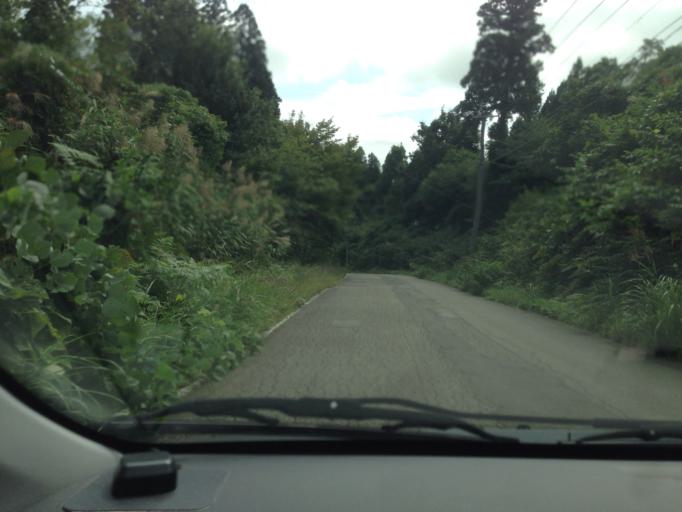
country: JP
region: Fukushima
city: Kitakata
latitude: 37.5034
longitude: 139.8200
